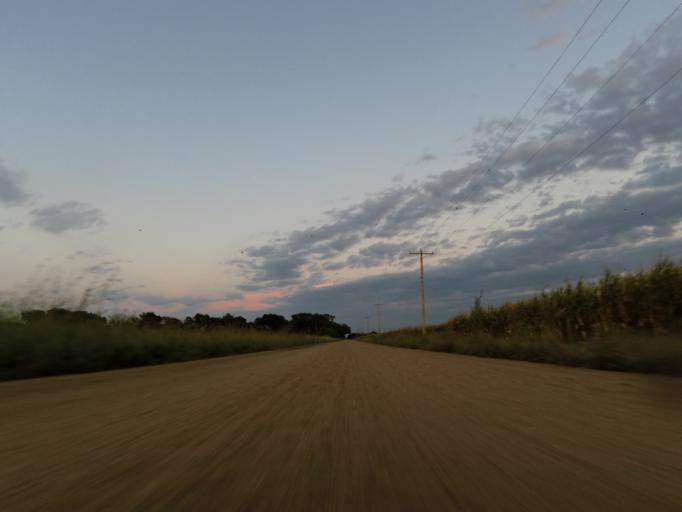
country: US
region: Kansas
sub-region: Reno County
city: South Hutchinson
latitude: 37.9555
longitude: -98.0366
